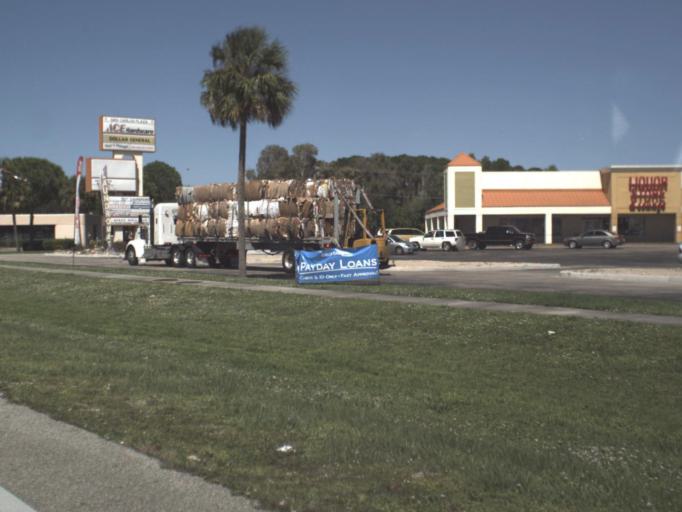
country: US
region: Florida
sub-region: Lee County
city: San Carlos Park
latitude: 26.4647
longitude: -81.8314
